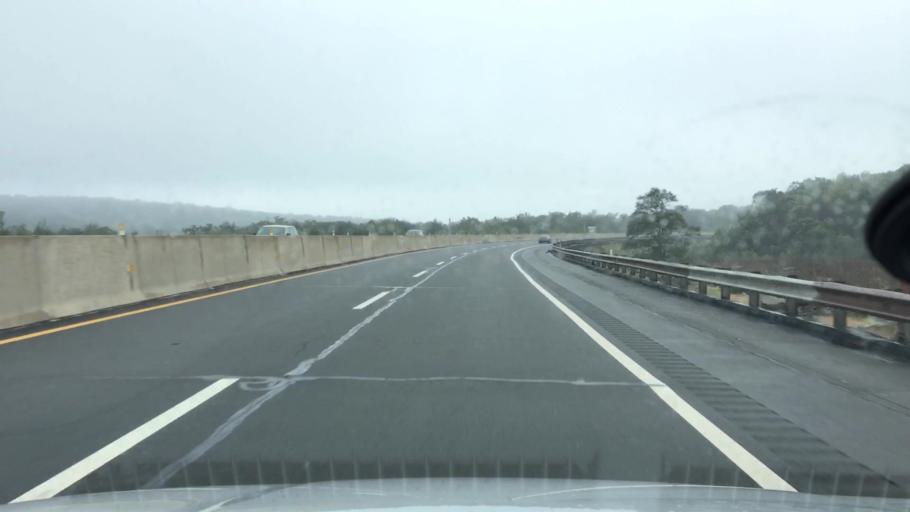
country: US
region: Pennsylvania
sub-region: Luzerne County
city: Georgetown
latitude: 41.2092
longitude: -75.8014
